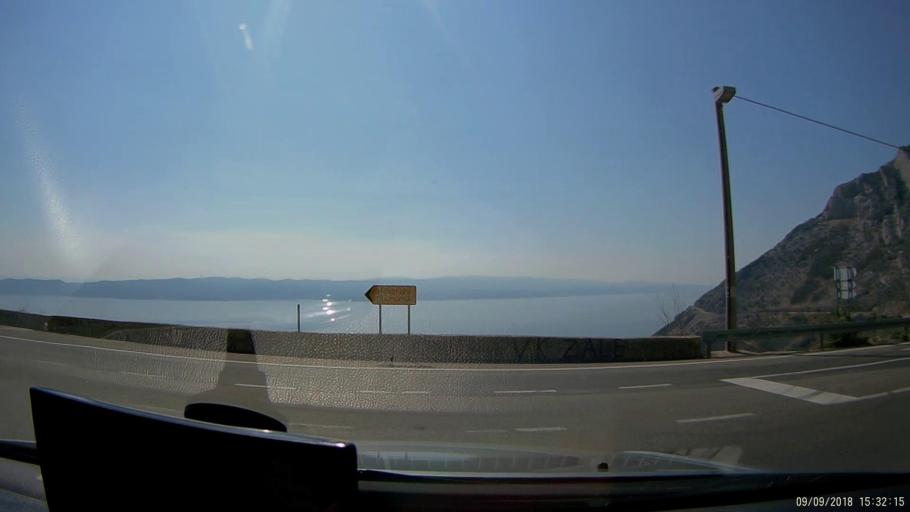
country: HR
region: Splitsko-Dalmatinska
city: Donja Brela
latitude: 43.4019
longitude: 16.8929
